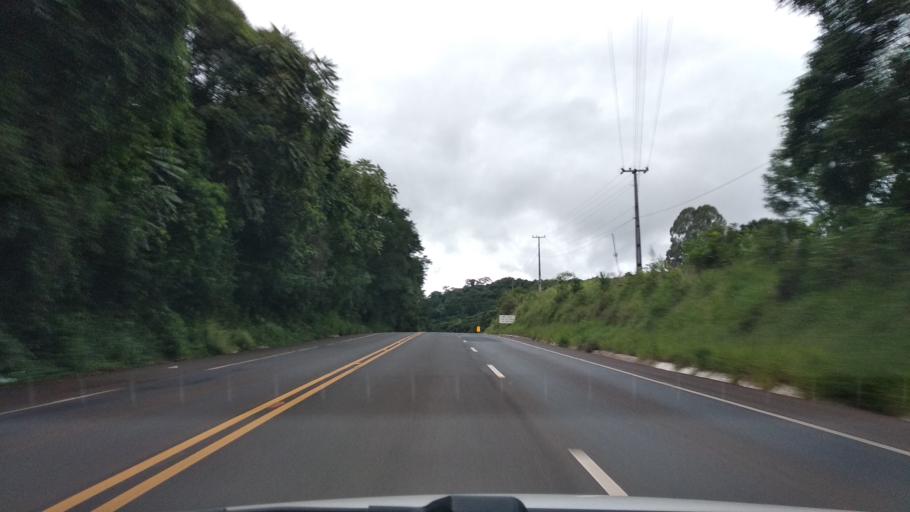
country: BR
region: Santa Catarina
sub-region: Videira
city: Videira
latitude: -27.0504
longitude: -51.2103
